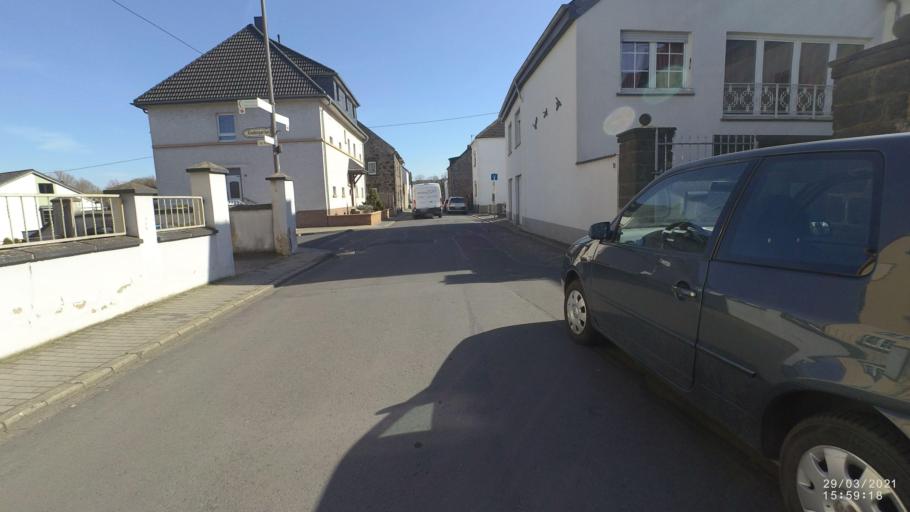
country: DE
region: Rheinland-Pfalz
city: Plaidt
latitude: 50.3896
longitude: 7.3932
